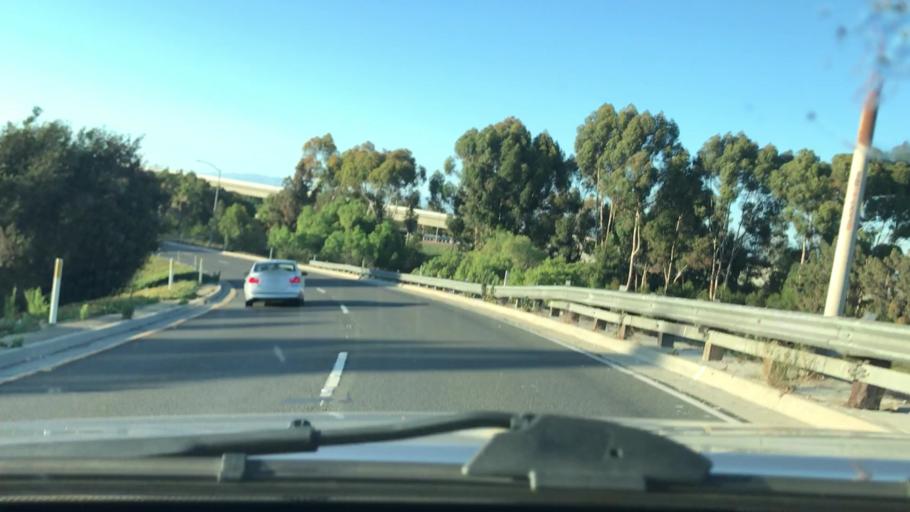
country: US
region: California
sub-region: Orange County
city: Rossmoor
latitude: 33.7753
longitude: -118.0905
